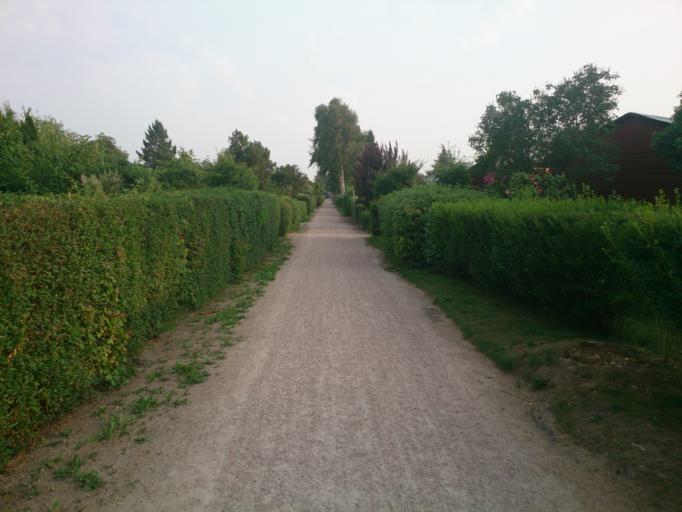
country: DE
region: Lower Saxony
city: Neu Wulmstorf
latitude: 53.5321
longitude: 9.8446
